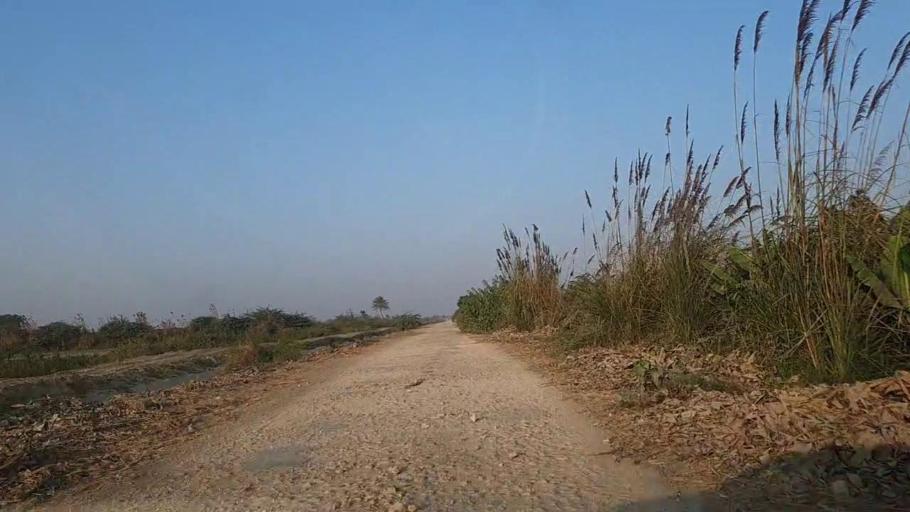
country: PK
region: Sindh
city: Keti Bandar
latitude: 24.2772
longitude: 67.6847
